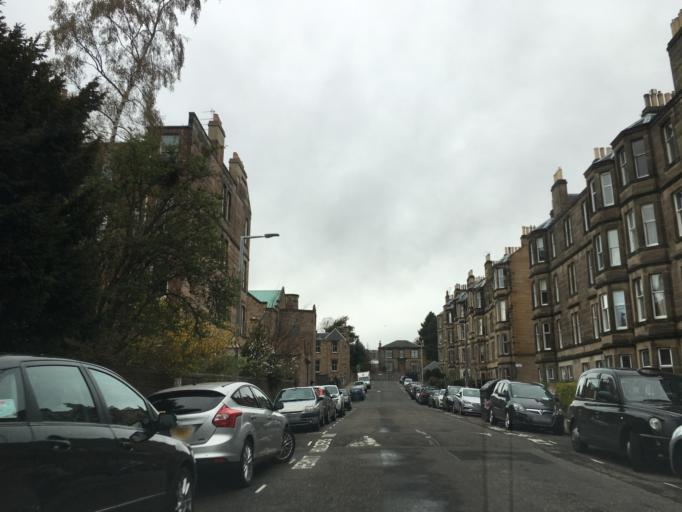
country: GB
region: Scotland
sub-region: Edinburgh
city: Edinburgh
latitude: 55.9297
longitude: -3.2054
